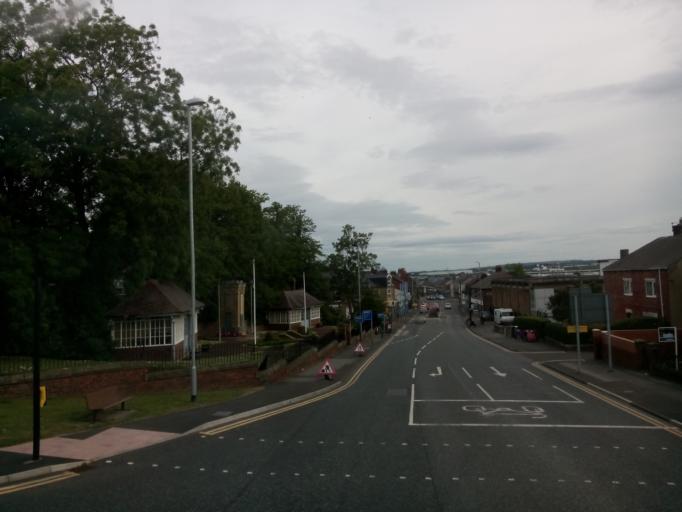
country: GB
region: England
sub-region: Gateshead
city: Lamesley
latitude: 54.8982
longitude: -1.5774
